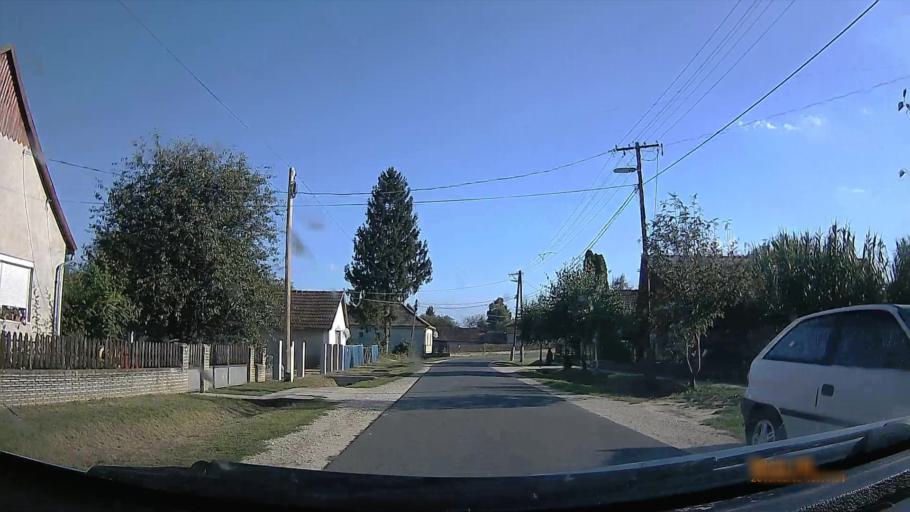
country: HU
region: Zala
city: Pacsa
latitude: 46.6278
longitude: 17.0573
